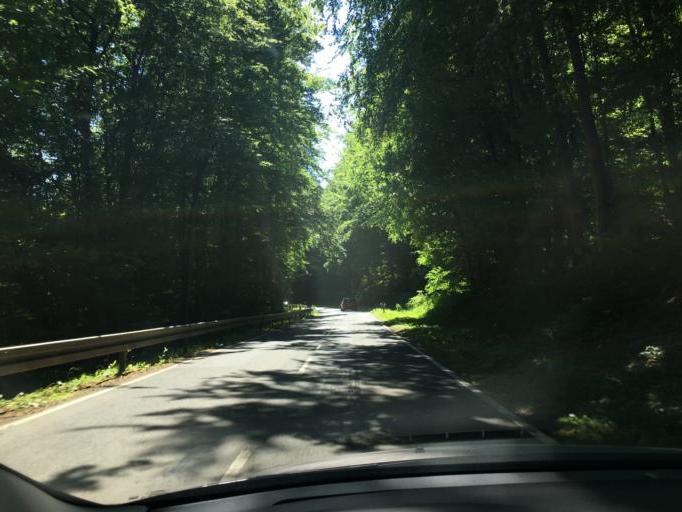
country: DE
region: Hesse
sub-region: Regierungsbezirk Kassel
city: Malsfeld
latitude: 51.0737
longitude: 9.5463
